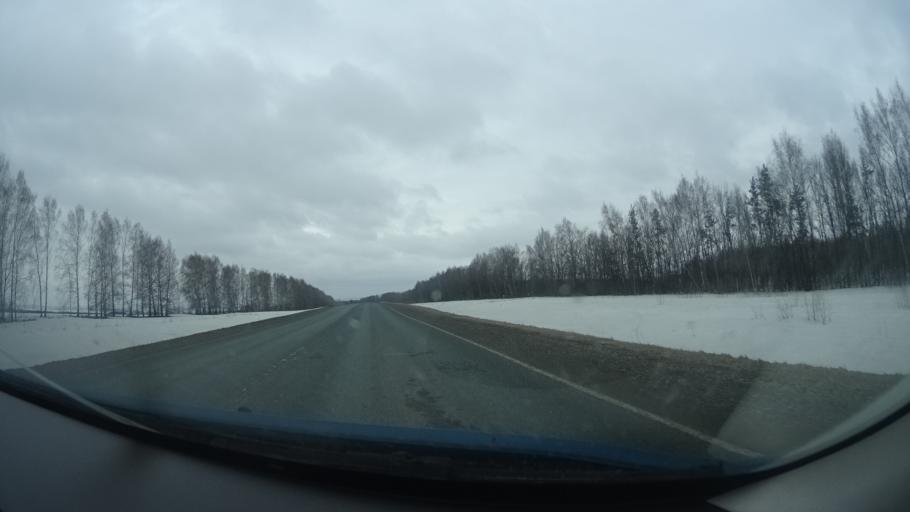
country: RU
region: Bashkortostan
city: Birsk
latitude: 55.2984
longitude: 55.6407
